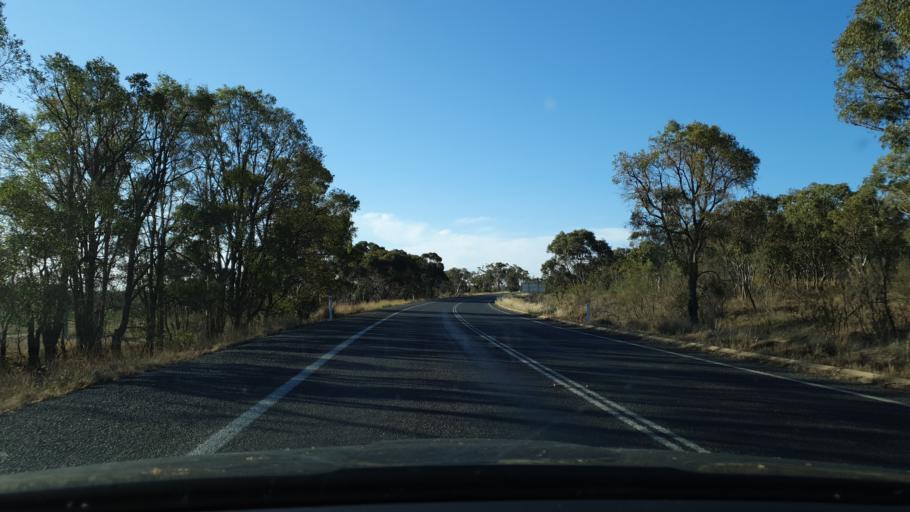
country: AU
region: Queensland
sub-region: Southern Downs
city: Stanthorpe
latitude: -28.6706
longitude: 151.9173
